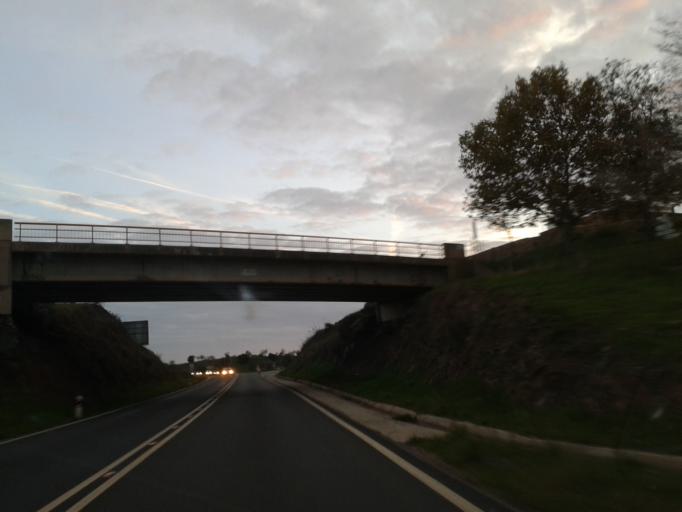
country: PT
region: Faro
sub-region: Castro Marim
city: Castro Marim
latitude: 37.2169
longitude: -7.4382
